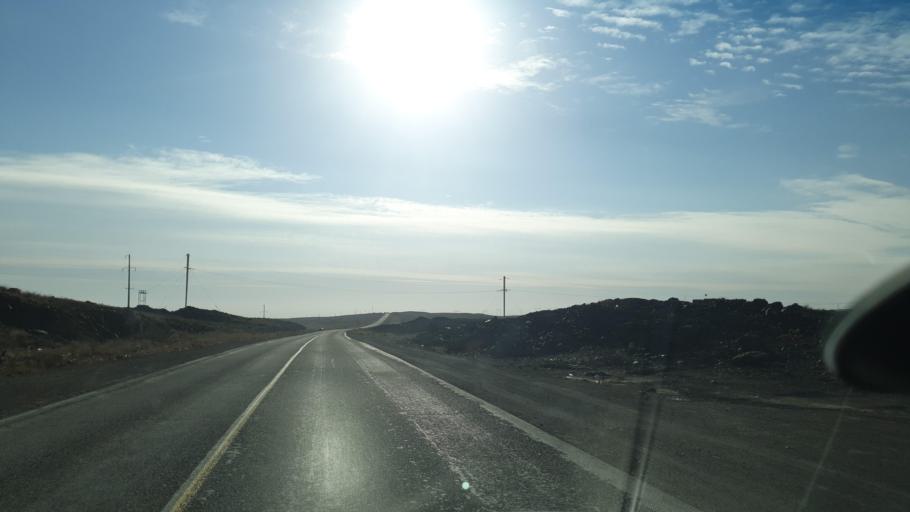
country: KZ
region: Zhambyl
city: Mynaral
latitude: 45.7210
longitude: 73.4033
